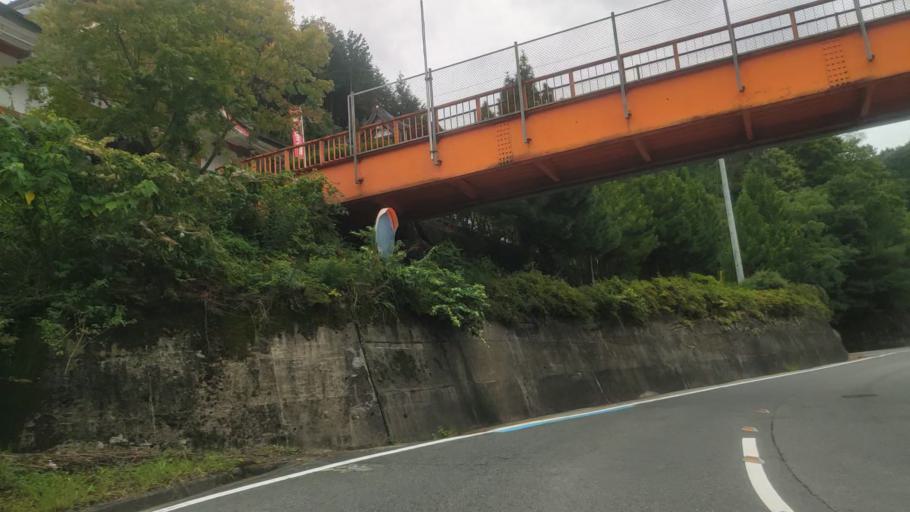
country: JP
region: Wakayama
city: Koya
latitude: 34.2181
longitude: 135.5379
